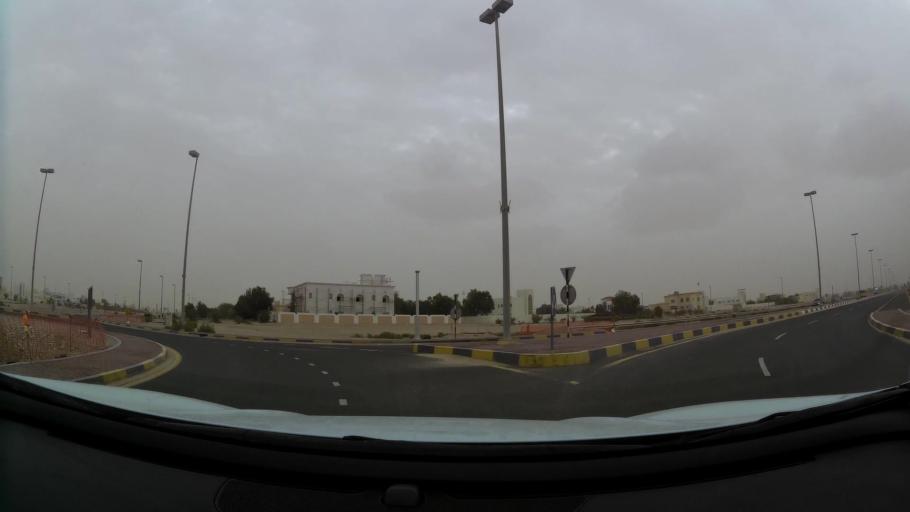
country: AE
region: Abu Dhabi
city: Abu Dhabi
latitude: 24.4234
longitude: 54.7312
